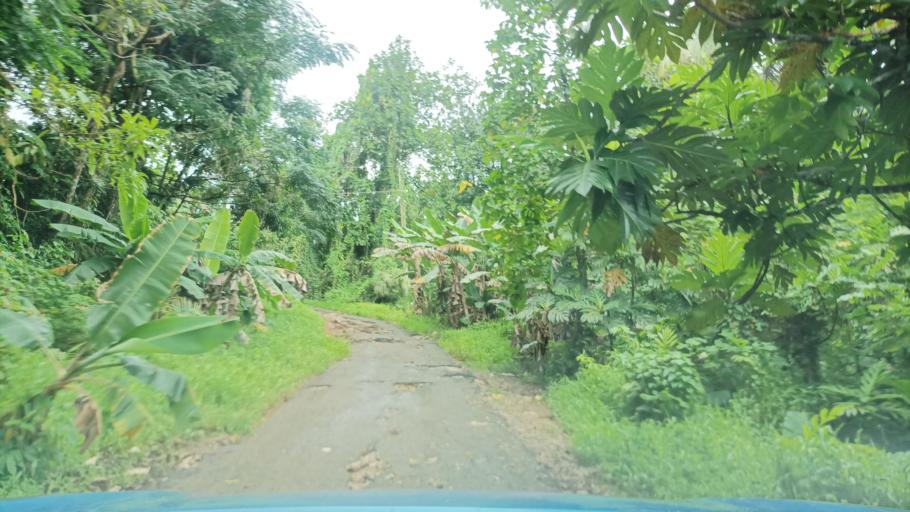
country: FM
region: Pohnpei
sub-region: Sokehs Municipality
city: Palikir - National Government Center
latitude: 6.8303
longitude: 158.1578
